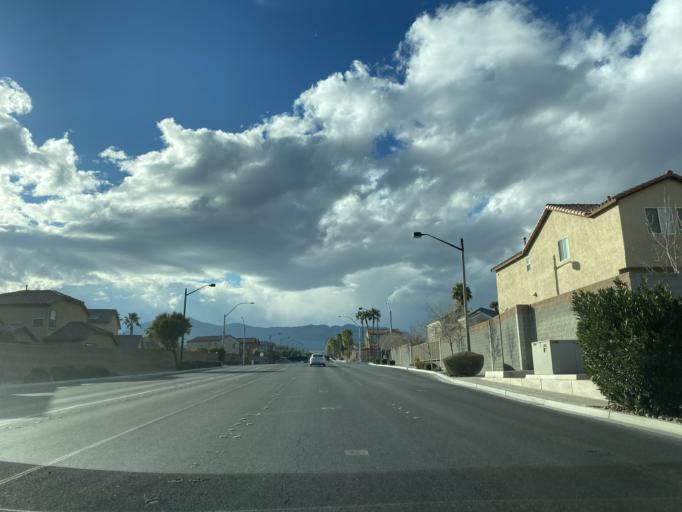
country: US
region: Nevada
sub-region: Clark County
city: Summerlin South
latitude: 36.2846
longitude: -115.2957
